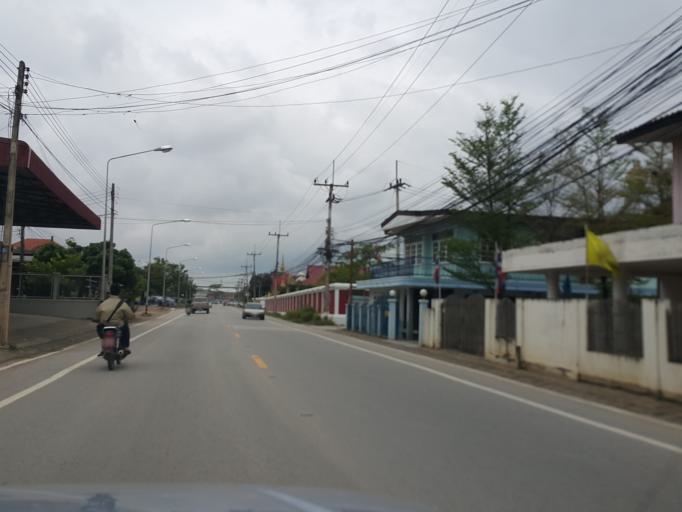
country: TH
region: Lamphun
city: Ban Thi
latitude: 18.5799
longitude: 99.0766
